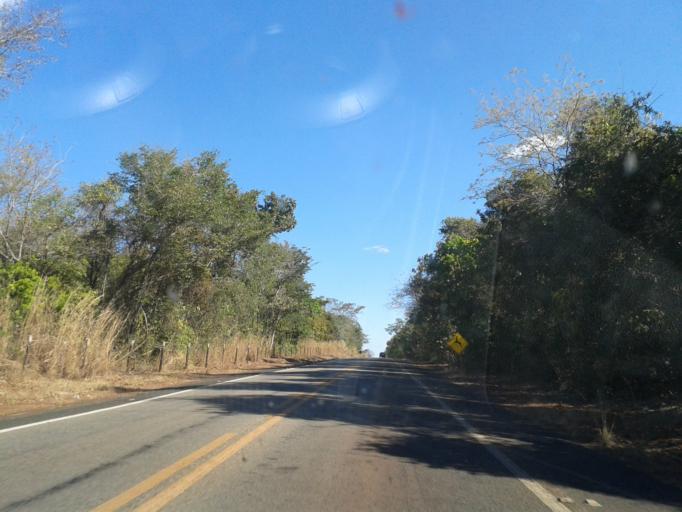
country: BR
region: Goias
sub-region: Mozarlandia
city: Mozarlandia
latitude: -14.6763
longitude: -50.5367
